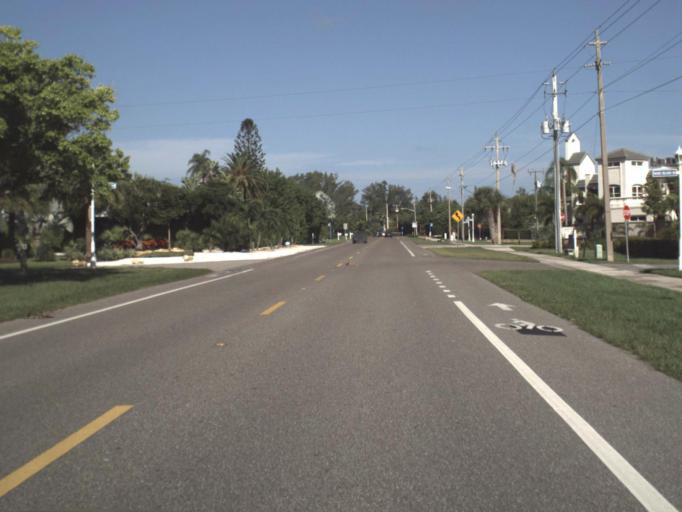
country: US
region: Florida
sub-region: Manatee County
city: Longboat Key
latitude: 27.4256
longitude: -82.6737
